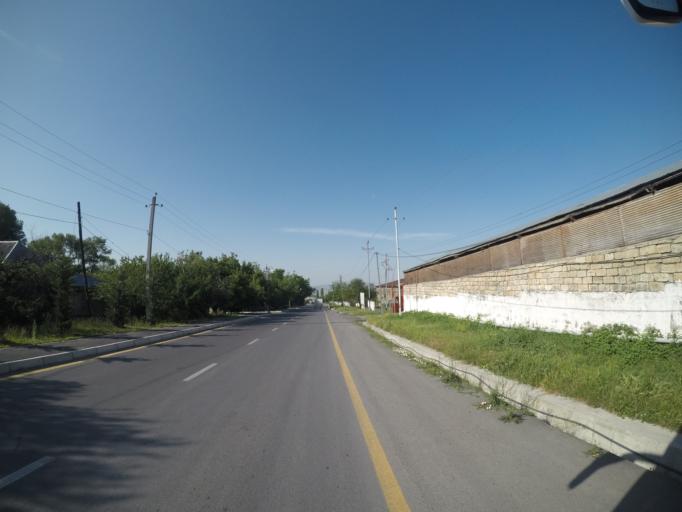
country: AZ
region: Shaki City
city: Sheki
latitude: 41.2152
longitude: 47.1681
